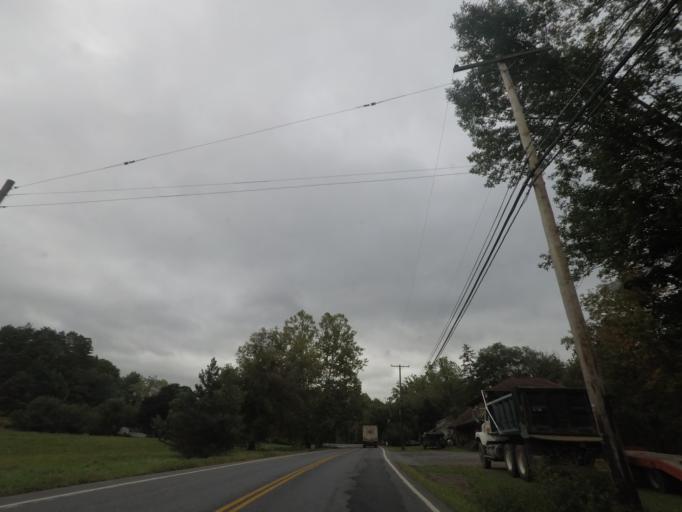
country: US
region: New York
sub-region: Rensselaer County
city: Hoosick Falls
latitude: 42.9309
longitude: -73.3533
